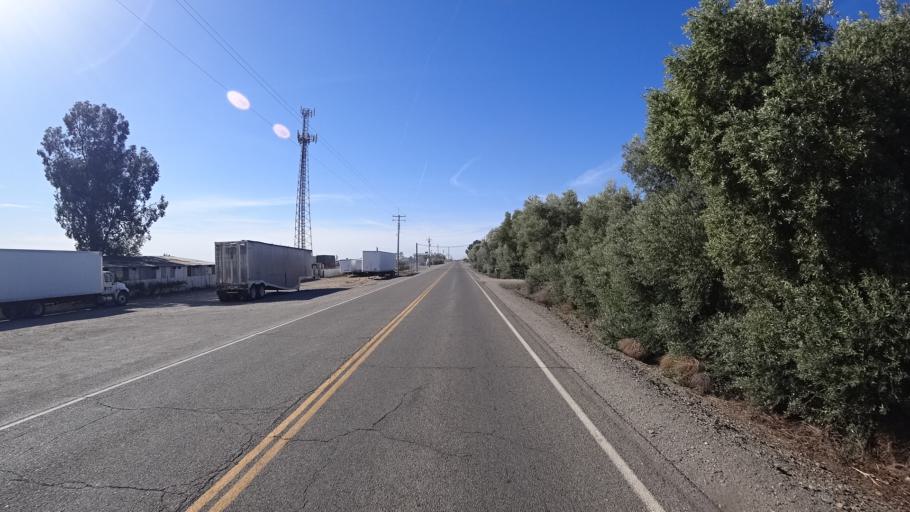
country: US
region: California
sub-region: Glenn County
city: Orland
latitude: 39.6950
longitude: -122.1966
